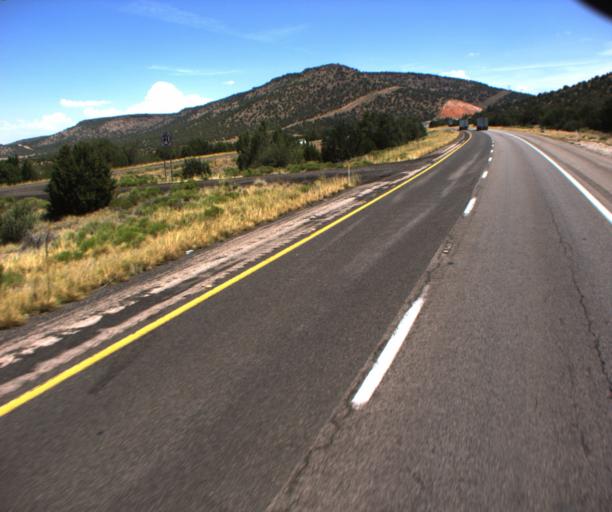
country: US
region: Arizona
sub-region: Mohave County
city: Peach Springs
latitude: 35.2779
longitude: -113.1306
